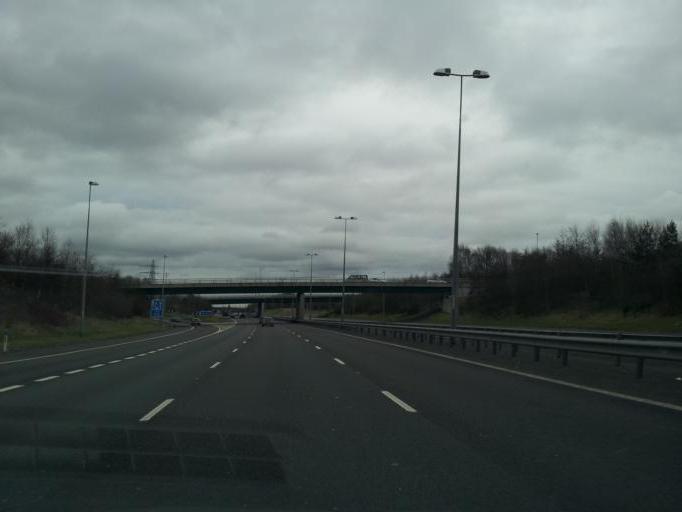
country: GB
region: England
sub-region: Staffordshire
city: Norton Canes
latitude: 52.6625
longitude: -1.9739
